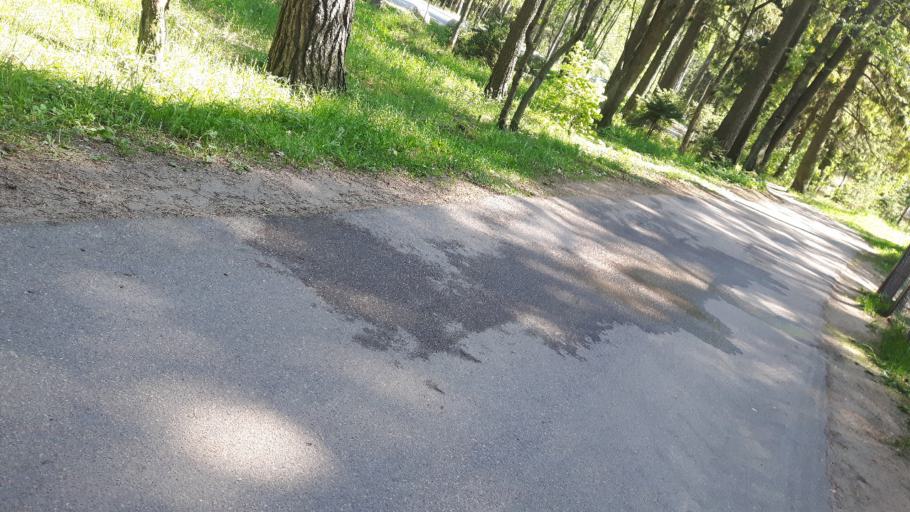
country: RU
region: St.-Petersburg
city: Komarovo
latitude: 60.1705
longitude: 29.8148
